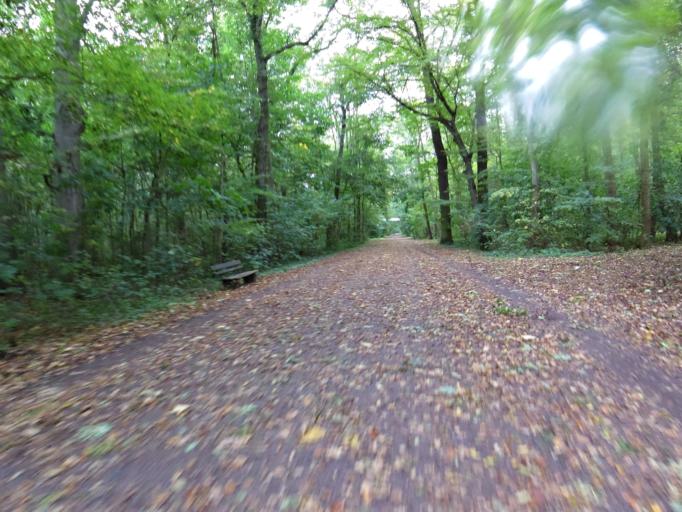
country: DE
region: Saxony
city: Markkleeberg
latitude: 51.2934
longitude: 12.3595
